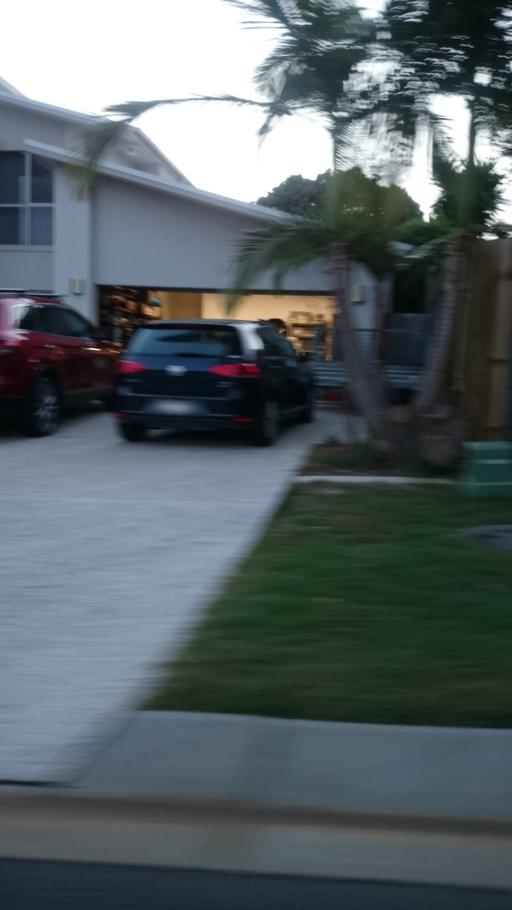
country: AU
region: Queensland
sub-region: Brisbane
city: Manly West
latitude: -27.4659
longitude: 153.1826
